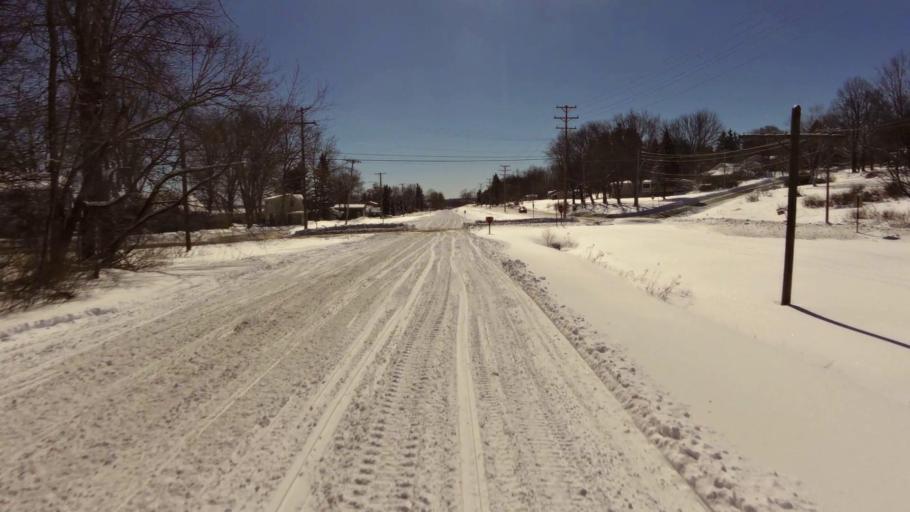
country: US
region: New York
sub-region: Chautauqua County
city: Mayville
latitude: 42.2551
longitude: -79.4940
